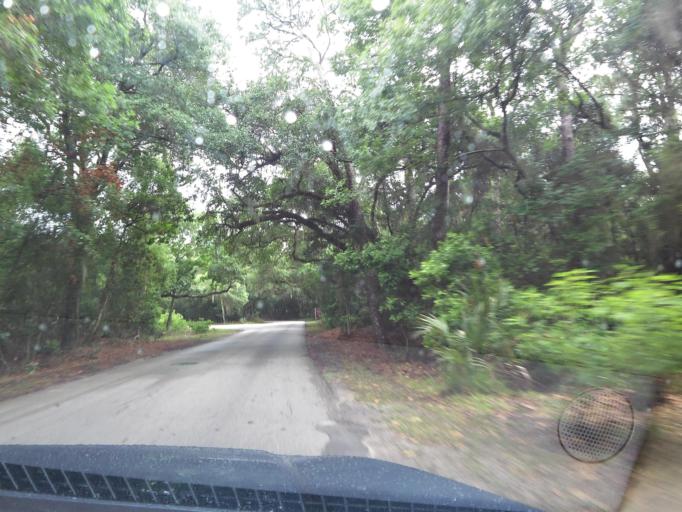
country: US
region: Florida
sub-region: Nassau County
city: Fernandina Beach
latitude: 30.6950
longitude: -81.4396
